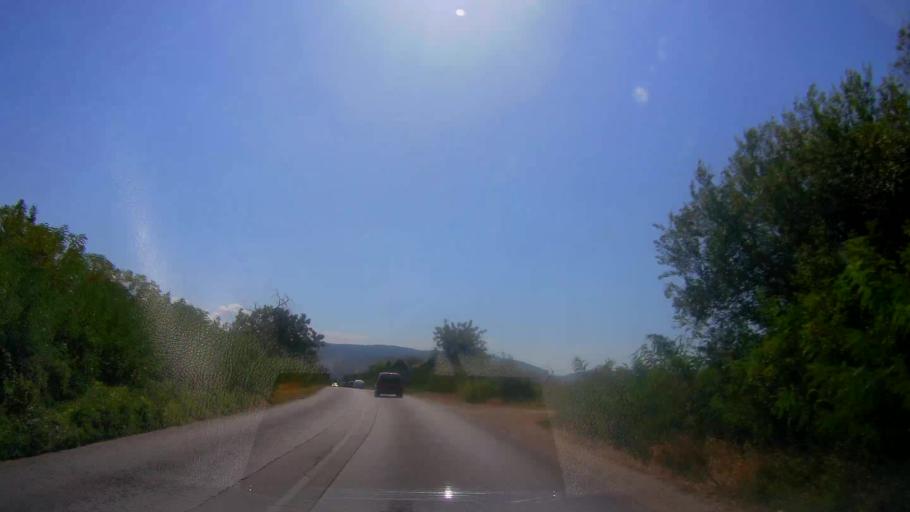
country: BG
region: Veliko Turnovo
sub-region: Obshtina Gorna Oryakhovitsa
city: Purvomaytsi
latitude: 43.1656
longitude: 25.6173
